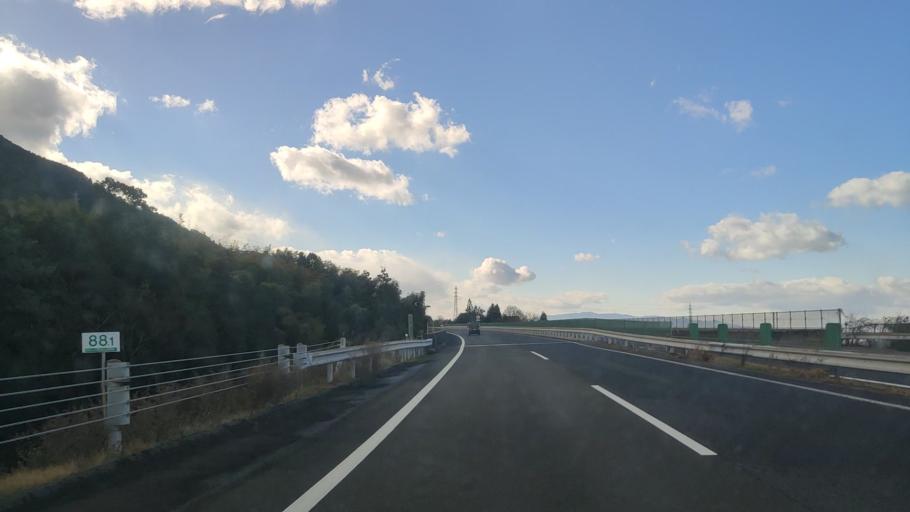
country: JP
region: Ehime
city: Niihama
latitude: 33.9173
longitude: 133.2906
